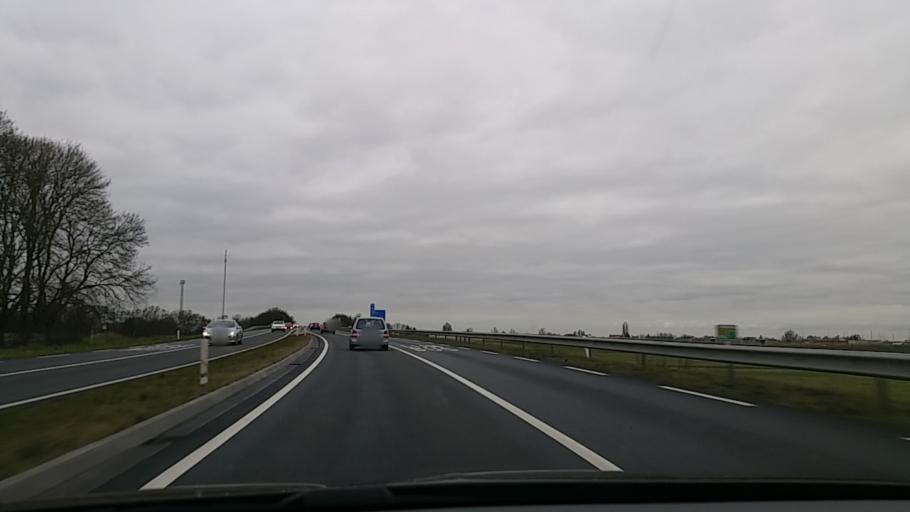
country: NL
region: South Holland
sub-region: Gemeente Kaag en Braassem
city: Leimuiden
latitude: 52.2191
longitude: 4.6810
